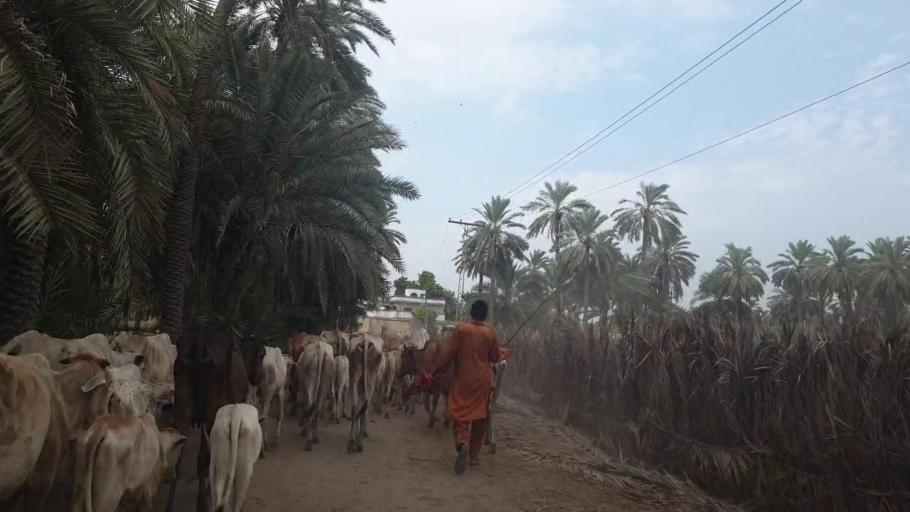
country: PK
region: Sindh
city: Sukkur
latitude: 27.6290
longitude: 68.7893
